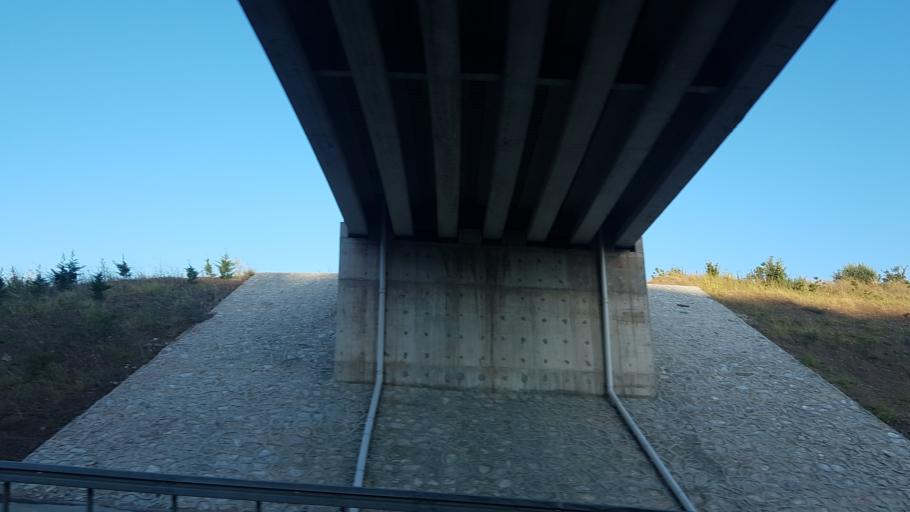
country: TR
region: Bursa
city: Umurbey
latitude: 40.3588
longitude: 29.1324
